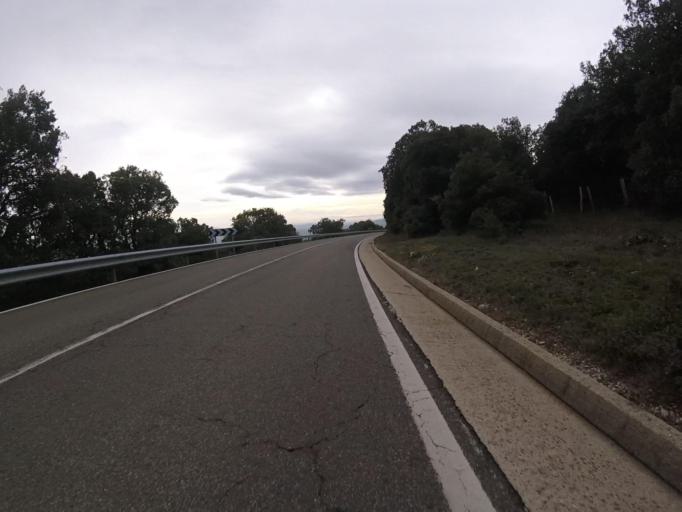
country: ES
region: Navarre
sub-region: Provincia de Navarra
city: Lezaun
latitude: 42.7562
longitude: -2.0114
